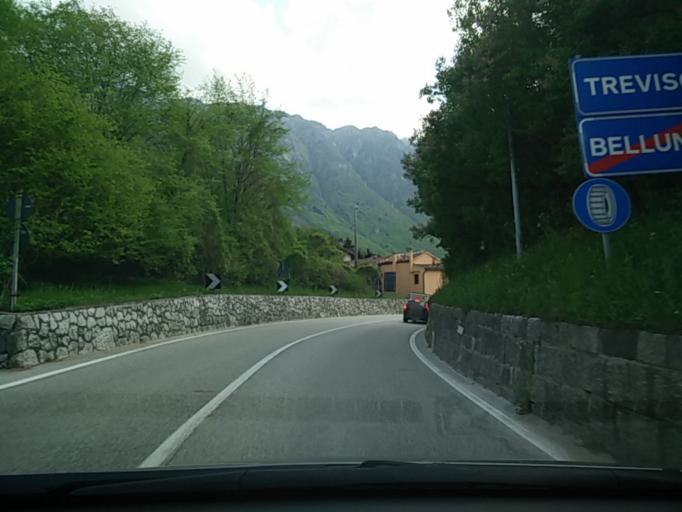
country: IT
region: Veneto
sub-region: Provincia di Belluno
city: Farra d'Alpago
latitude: 46.0802
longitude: 12.3366
